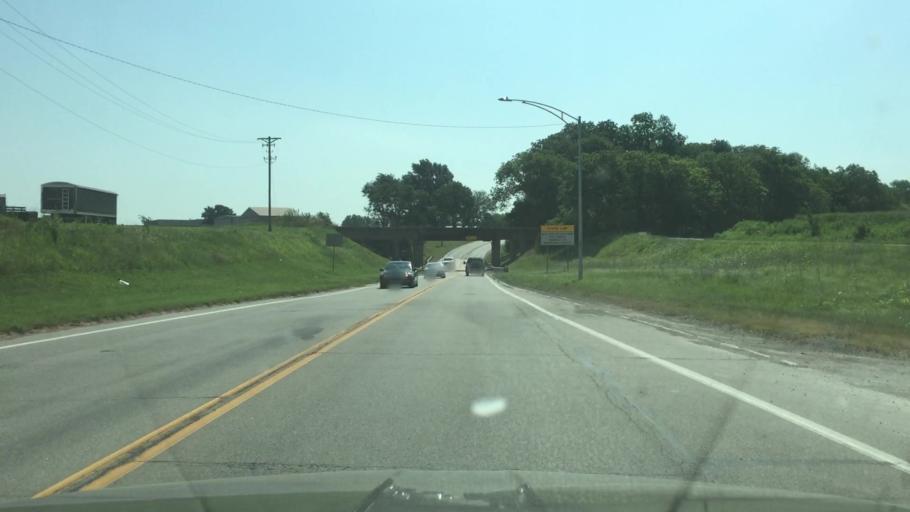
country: US
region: Missouri
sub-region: Pettis County
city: Sedalia
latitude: 38.6998
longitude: -93.1886
